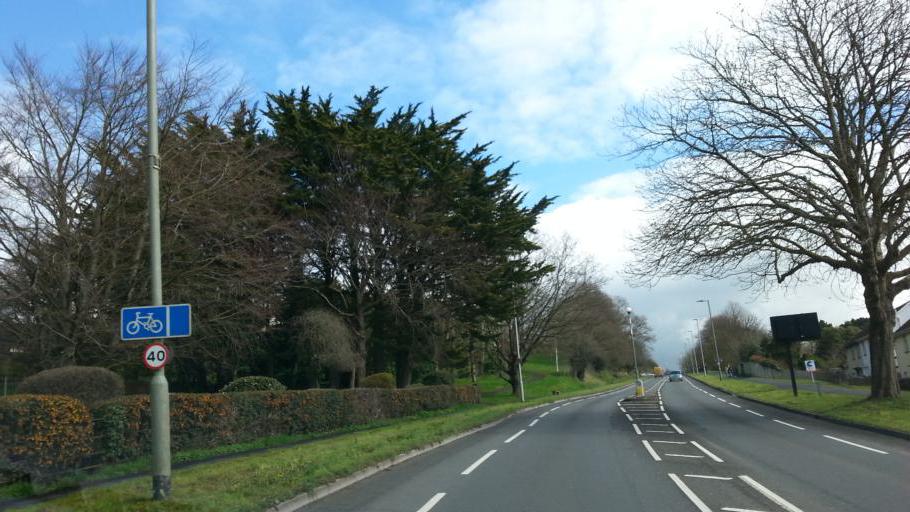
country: GB
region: England
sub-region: Devon
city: Barnstaple
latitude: 51.0868
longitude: -4.0600
